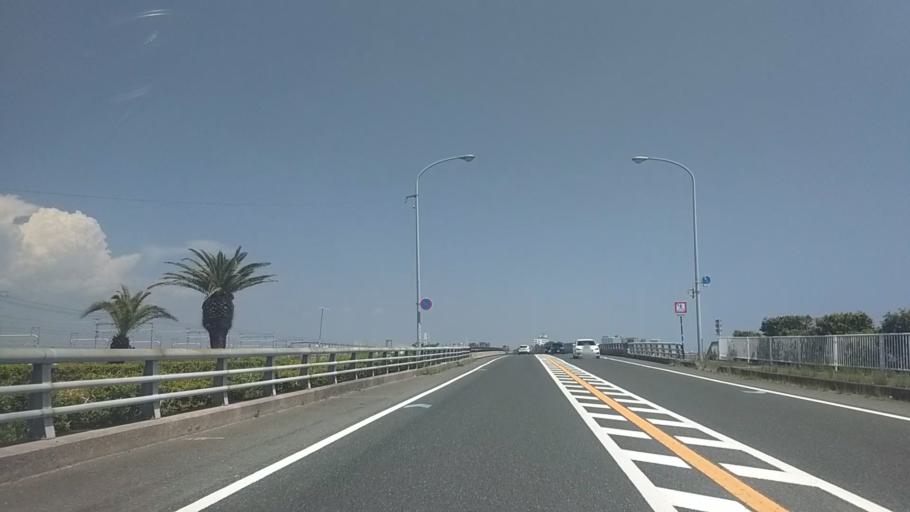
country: JP
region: Shizuoka
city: Kosai-shi
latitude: 34.6940
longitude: 137.5835
